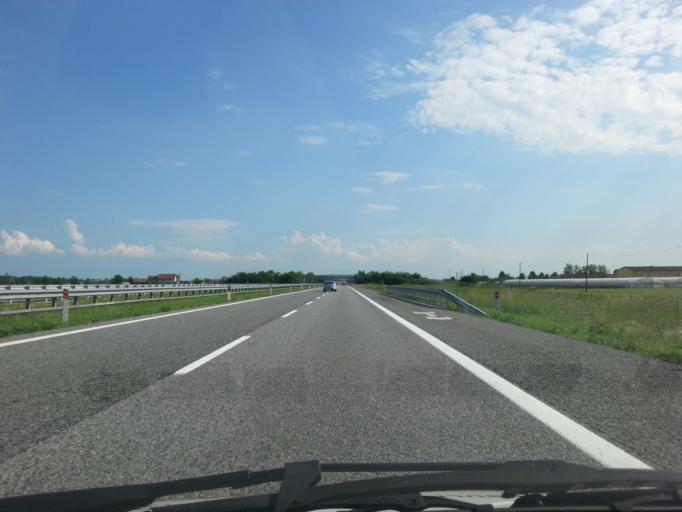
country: IT
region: Piedmont
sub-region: Provincia di Torino
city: Carmagnola
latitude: 44.8331
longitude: 7.7499
